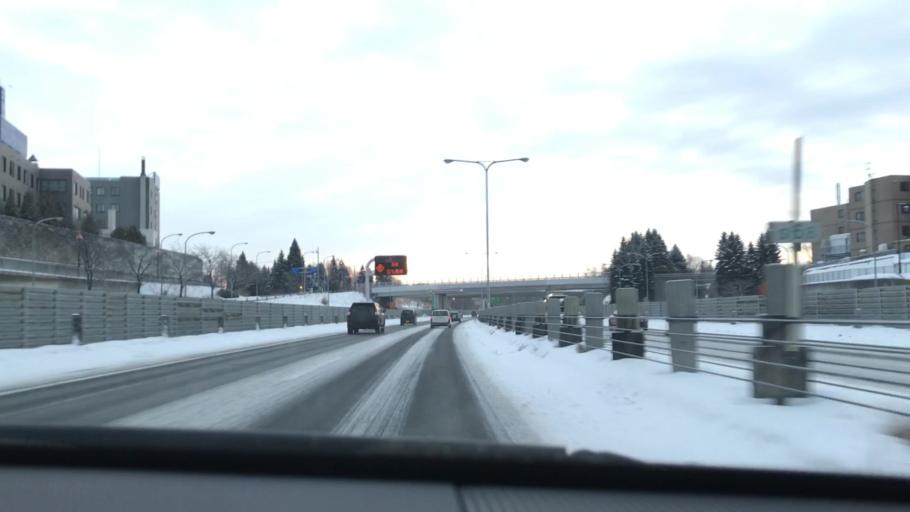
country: JP
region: Hokkaido
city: Sapporo
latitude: 43.0230
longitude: 141.4562
